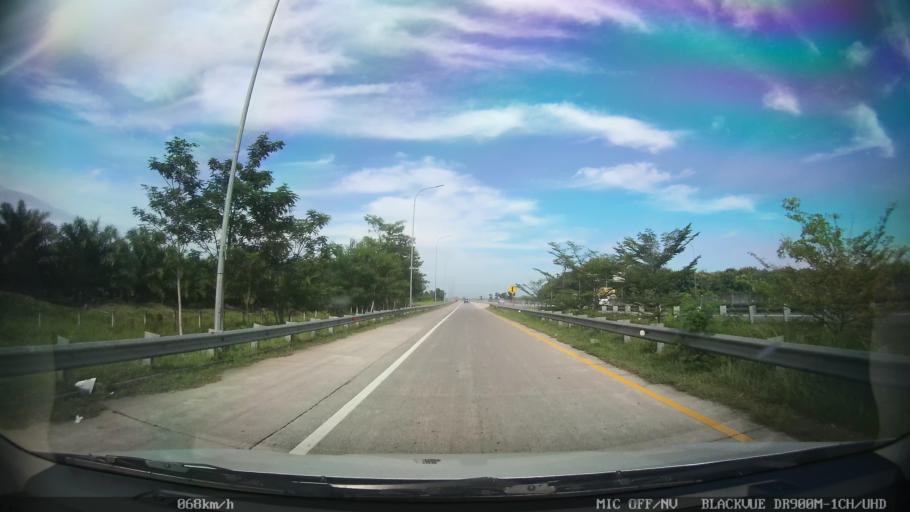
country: ID
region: North Sumatra
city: Medan
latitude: 3.6376
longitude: 98.6354
